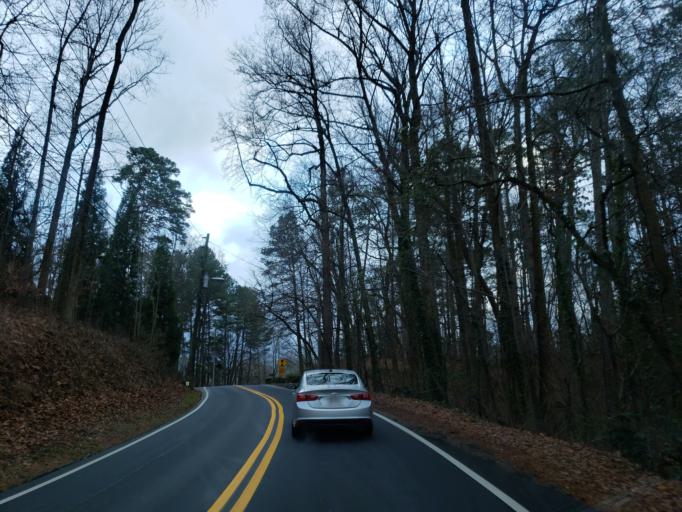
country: US
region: Georgia
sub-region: Fulton County
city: Sandy Springs
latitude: 33.9372
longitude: -84.4091
